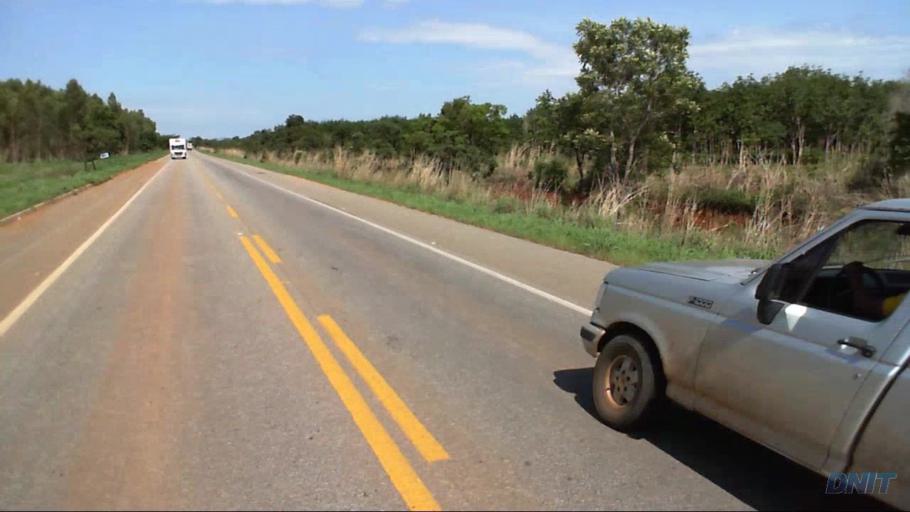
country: BR
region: Goias
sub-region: Barro Alto
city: Barro Alto
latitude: -15.2059
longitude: -48.7230
